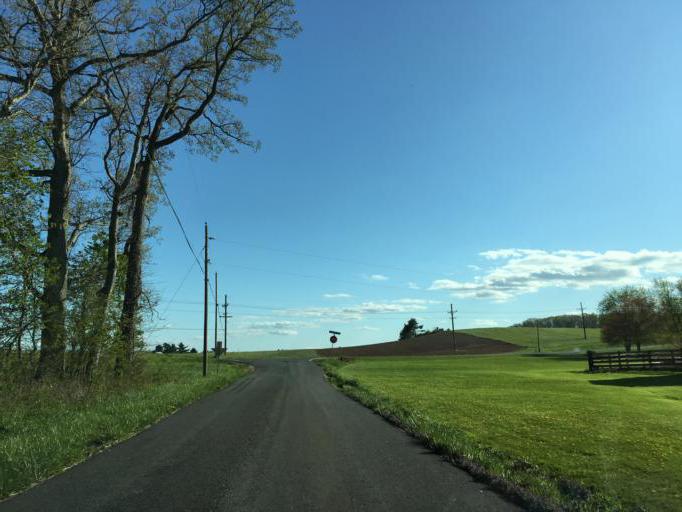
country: US
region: Maryland
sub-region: Frederick County
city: Woodsboro
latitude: 39.5702
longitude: -77.2395
